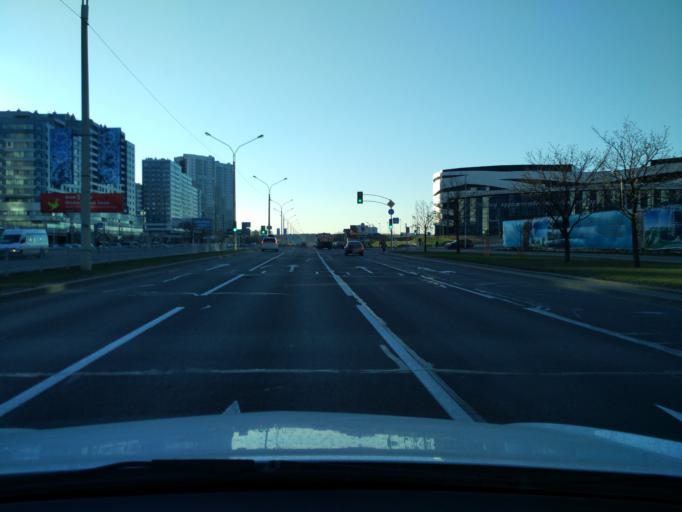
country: BY
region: Minsk
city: Zhdanovichy
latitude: 53.9403
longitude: 27.4703
